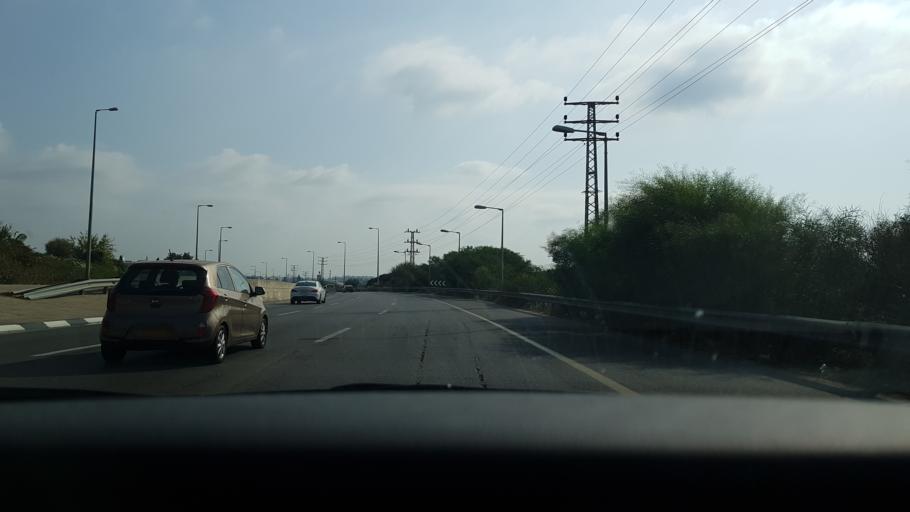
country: IL
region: Central District
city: Ness Ziona
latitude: 31.9211
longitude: 34.7806
